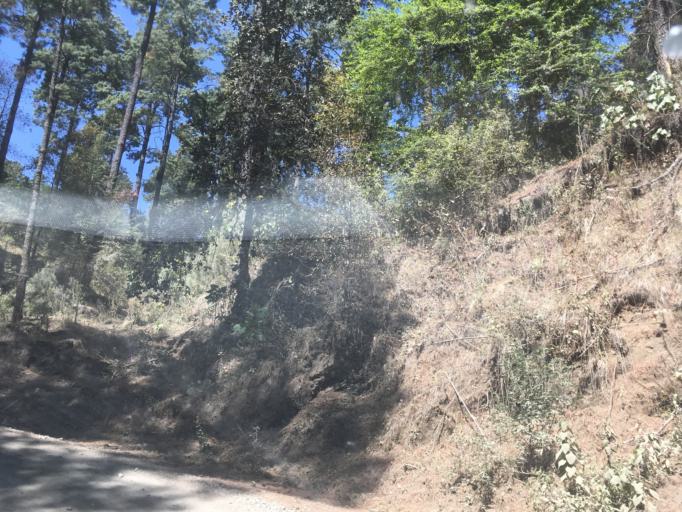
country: MX
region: Michoacan
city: Nuevo San Juan Parangaricutiro
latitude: 19.4590
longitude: -102.2039
